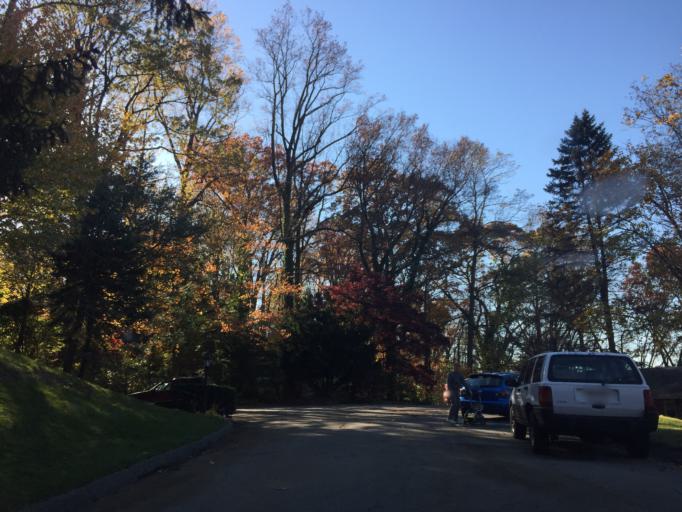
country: US
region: Maryland
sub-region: Baltimore County
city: Parkville
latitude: 39.4056
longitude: -76.5562
